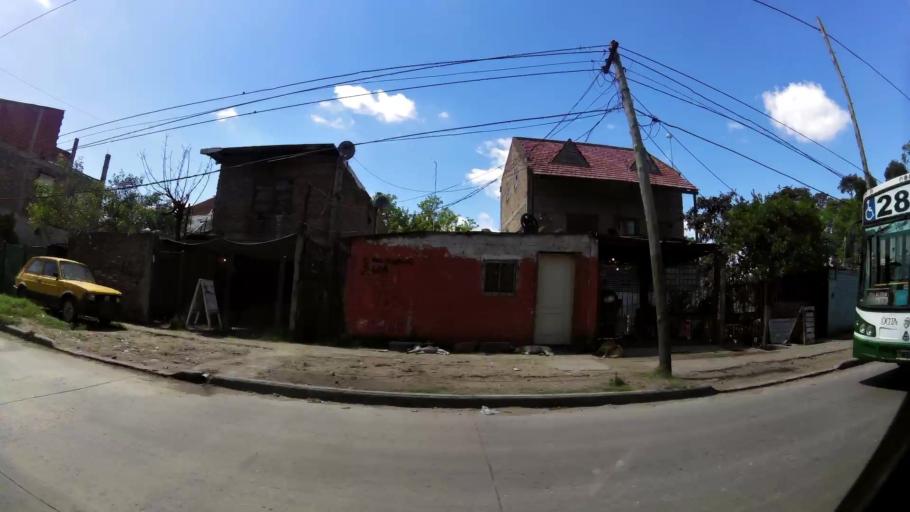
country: AR
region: Buenos Aires F.D.
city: Villa Lugano
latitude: -34.6756
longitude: -58.4352
